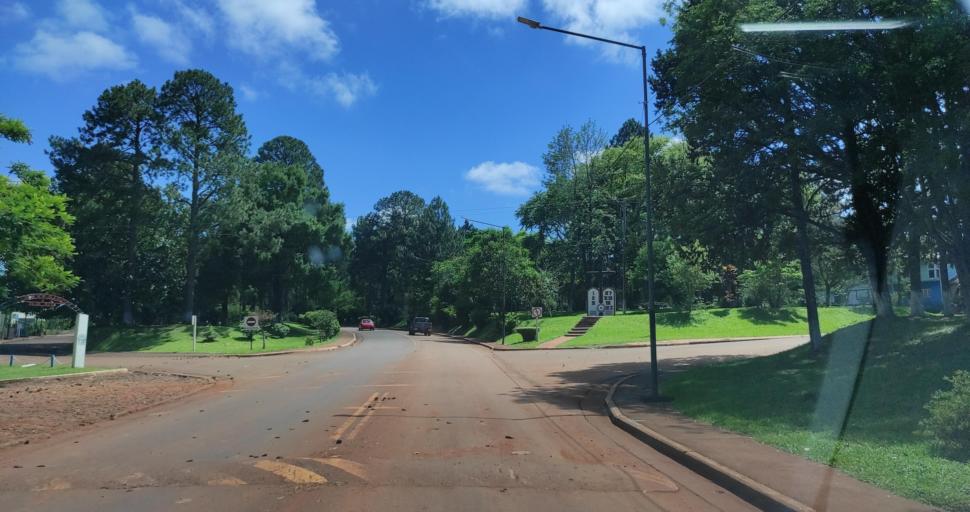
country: AR
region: Misiones
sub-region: Departamento de Veinticinco de Mayo
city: Veinticinco de Mayo
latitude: -27.3847
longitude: -54.7455
